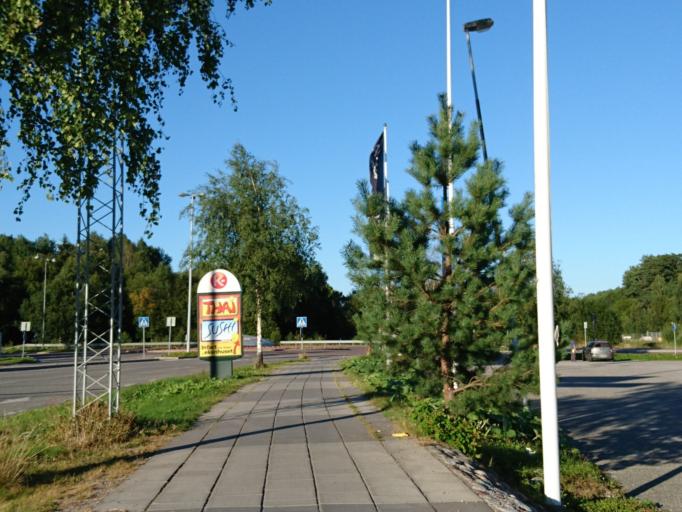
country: SE
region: Stockholm
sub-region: Huddinge Kommun
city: Segeltorp
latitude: 59.2697
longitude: 17.9220
